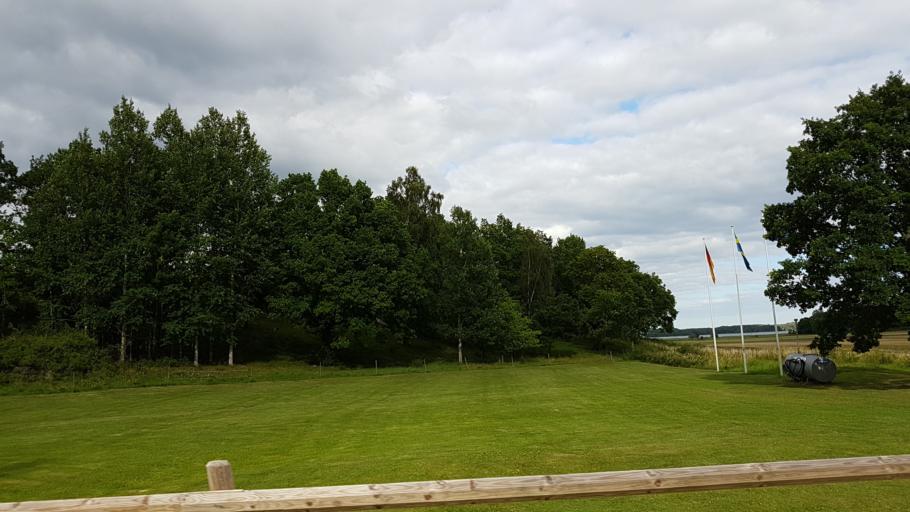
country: SE
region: OEstergoetland
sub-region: Valdemarsviks Kommun
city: Gusum
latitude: 58.4343
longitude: 16.5999
